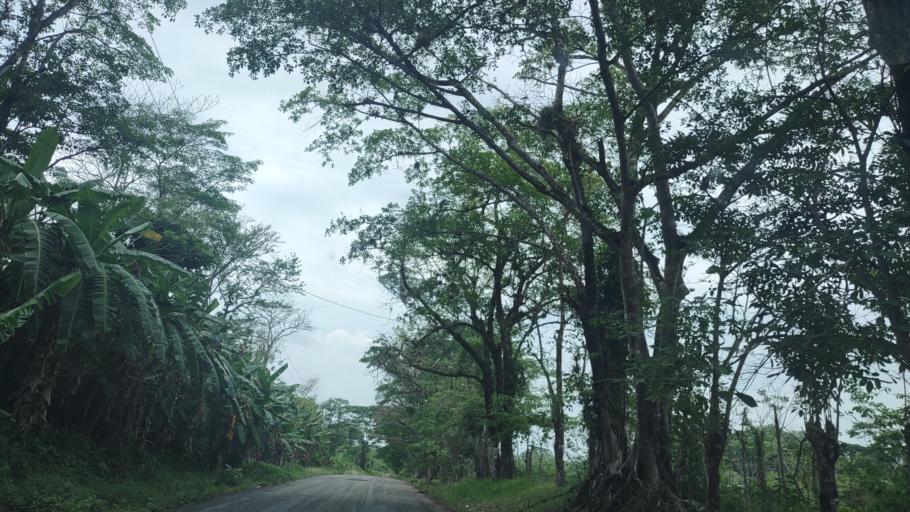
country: MX
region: Tabasco
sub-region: Huimanguillo
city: Francisco Rueda
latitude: 17.5414
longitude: -94.1277
